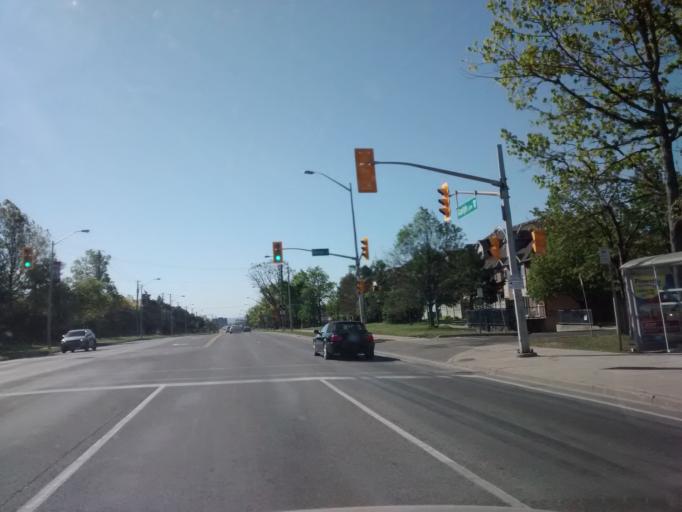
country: CA
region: Ontario
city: Burlington
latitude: 43.3615
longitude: -79.8171
